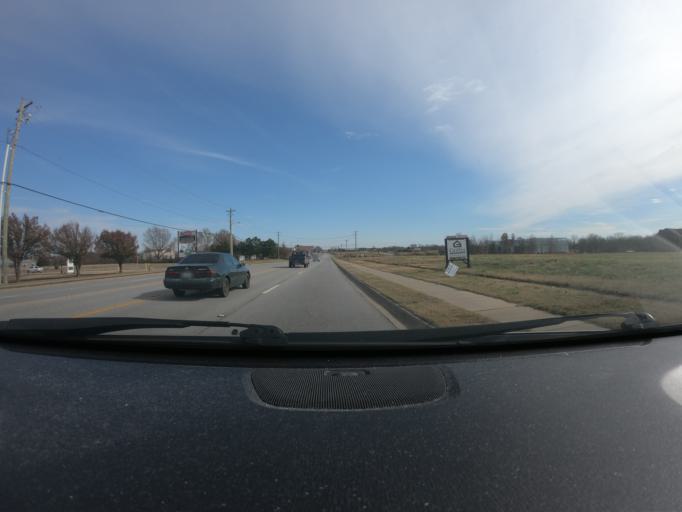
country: US
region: Arkansas
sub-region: Benton County
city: Bentonville
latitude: 36.3356
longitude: -94.2093
